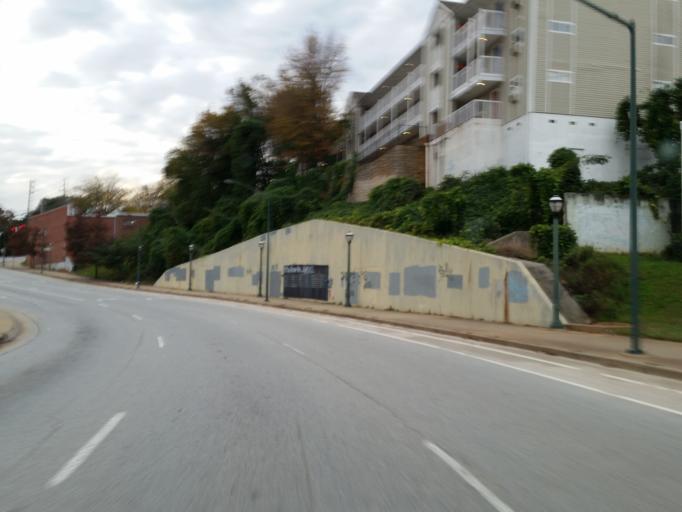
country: US
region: Georgia
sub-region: Fulton County
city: Atlanta
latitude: 33.7918
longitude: -84.4059
